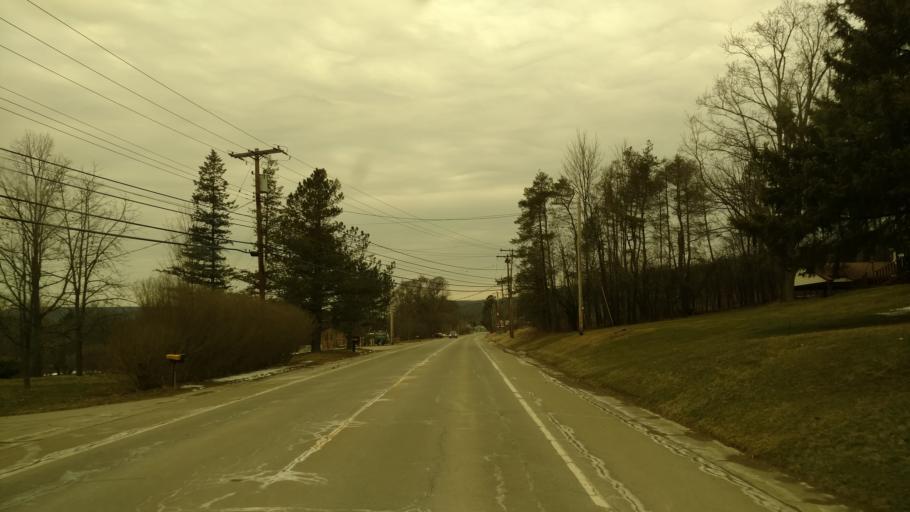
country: US
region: New York
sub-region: Allegany County
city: Wellsville
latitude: 42.1037
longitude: -77.9275
